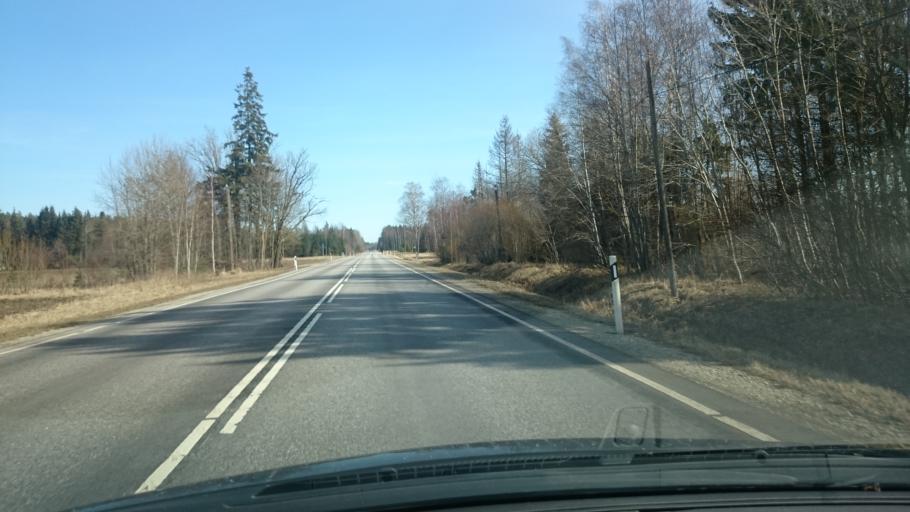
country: EE
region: Paernumaa
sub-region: Vaendra vald (alev)
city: Vandra
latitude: 58.6664
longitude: 25.1564
